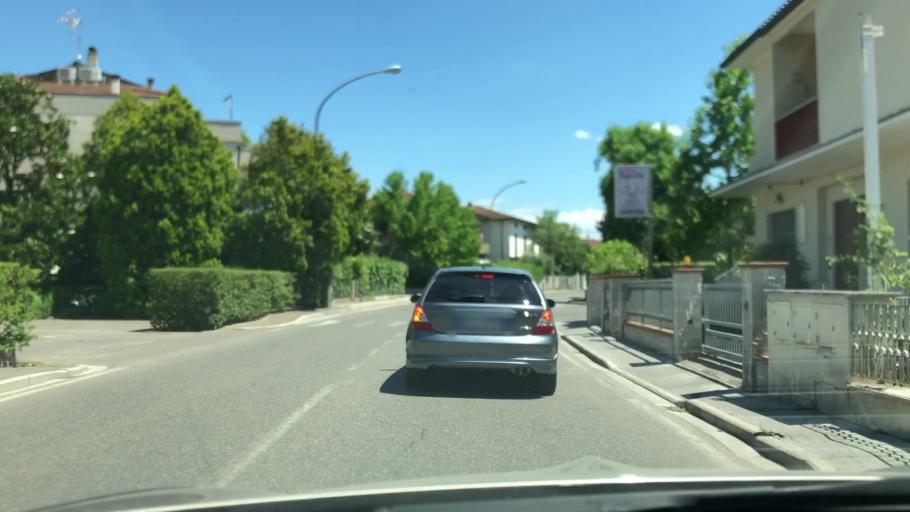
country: IT
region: Tuscany
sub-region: Province of Pisa
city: Ponsacco
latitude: 43.6179
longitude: 10.6373
